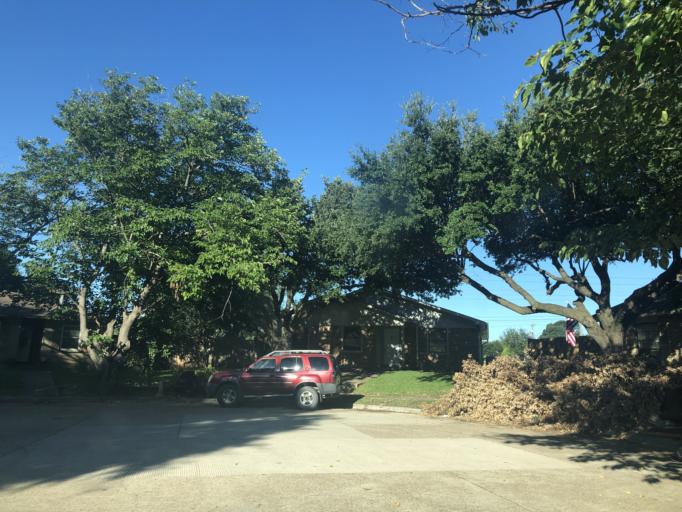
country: US
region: Texas
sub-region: Dallas County
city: Duncanville
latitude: 32.6362
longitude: -96.9495
